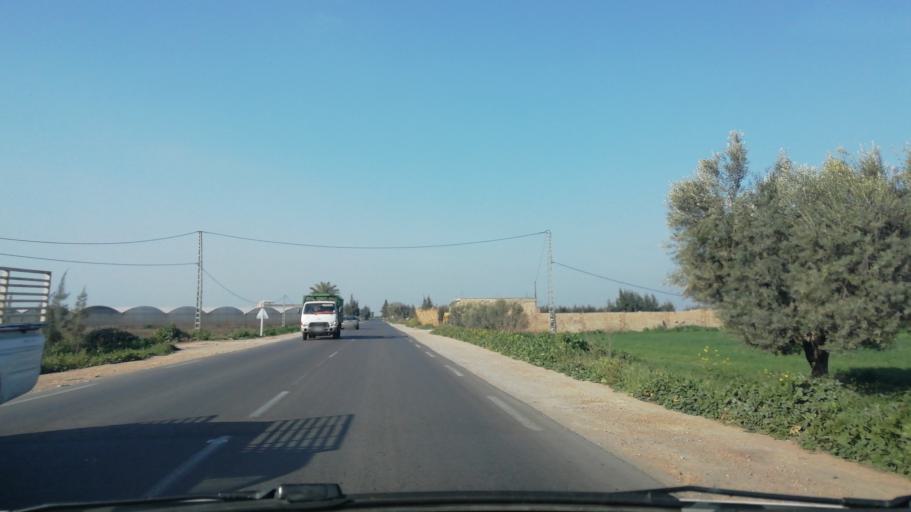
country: DZ
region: Mostaganem
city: Mostaganem
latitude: 35.7491
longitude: 0.1645
